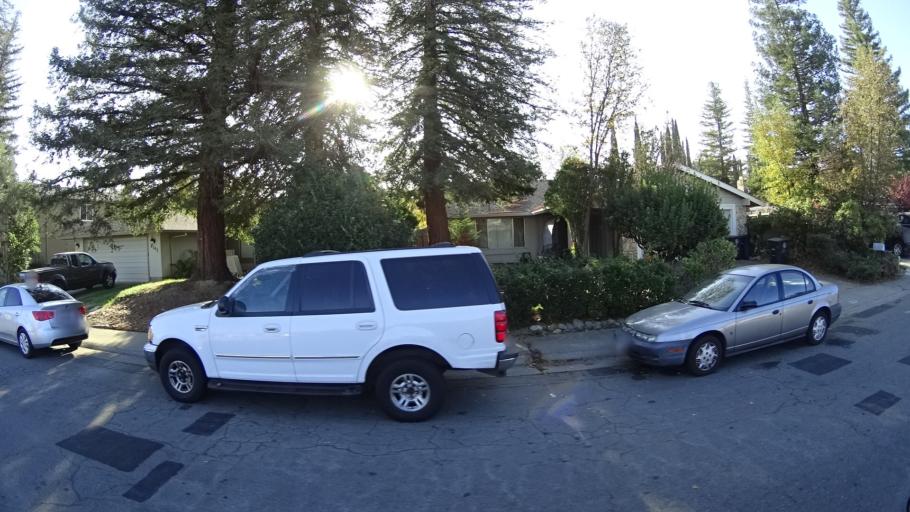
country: US
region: California
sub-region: Sacramento County
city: Citrus Heights
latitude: 38.7105
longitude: -121.2584
